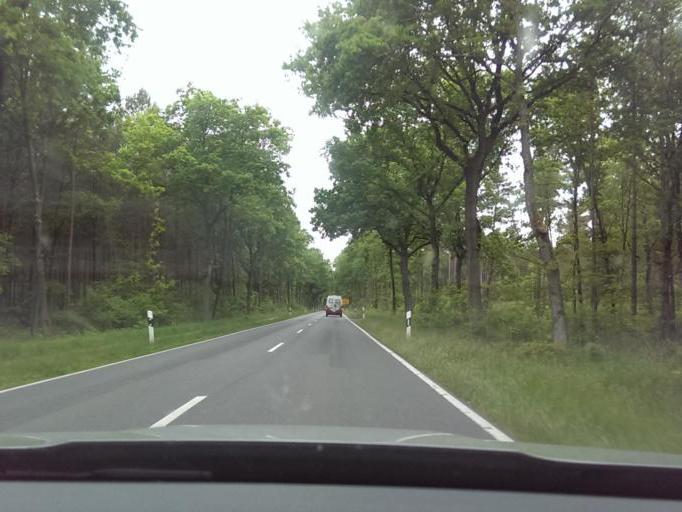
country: DE
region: Lower Saxony
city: Essel
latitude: 52.6979
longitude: 9.6698
